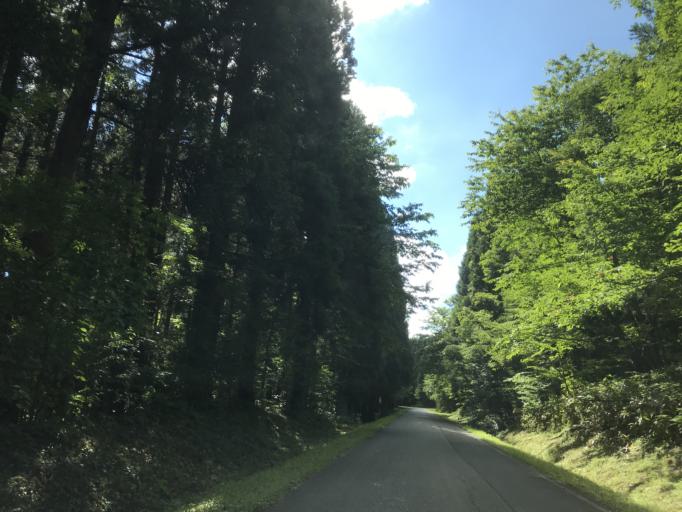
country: JP
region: Iwate
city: Ichinoseki
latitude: 38.9265
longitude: 140.9350
